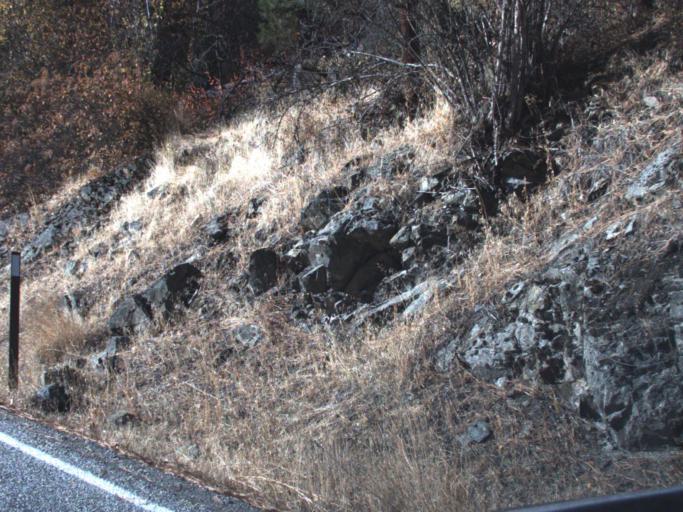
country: CA
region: British Columbia
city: Grand Forks
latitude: 48.9826
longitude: -118.5217
